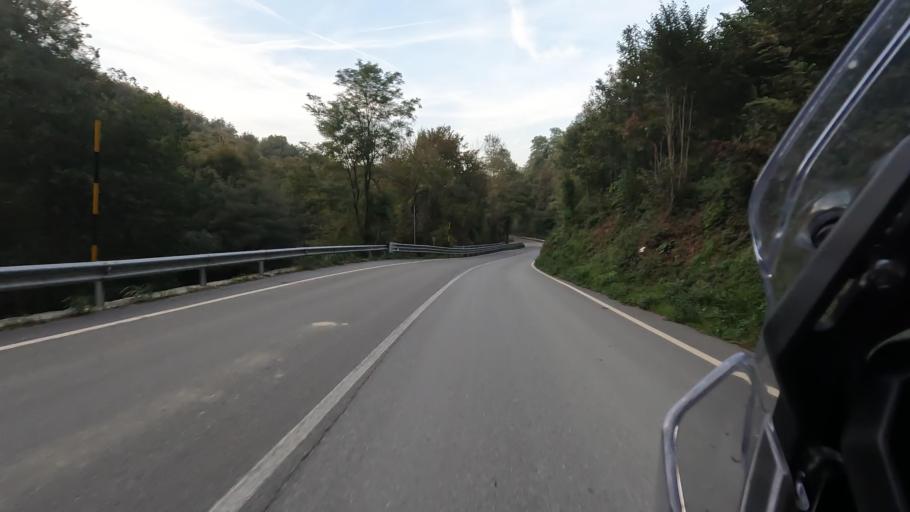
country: IT
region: Liguria
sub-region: Provincia di Savona
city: Sassello
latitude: 44.4606
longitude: 8.4817
